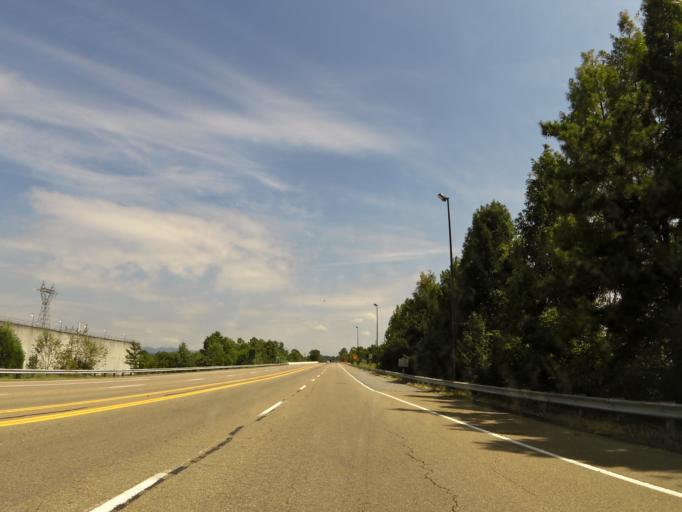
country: US
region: Tennessee
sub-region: Sullivan County
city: Kingsport
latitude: 36.5271
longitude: -82.5571
